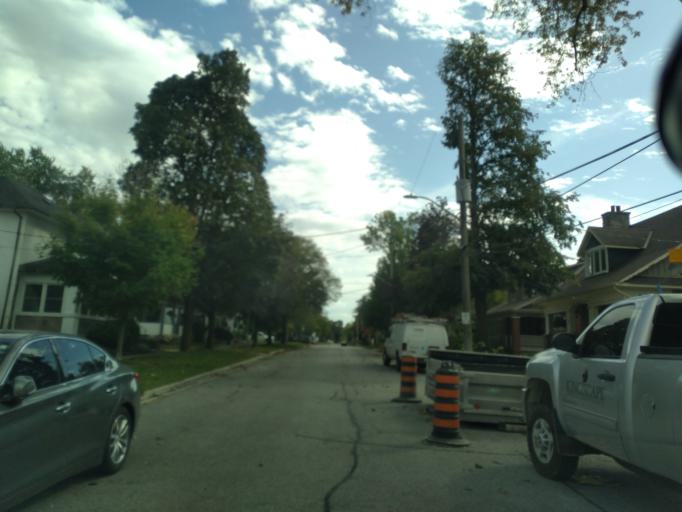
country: CA
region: Ontario
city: Newmarket
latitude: 43.9997
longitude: -79.4638
